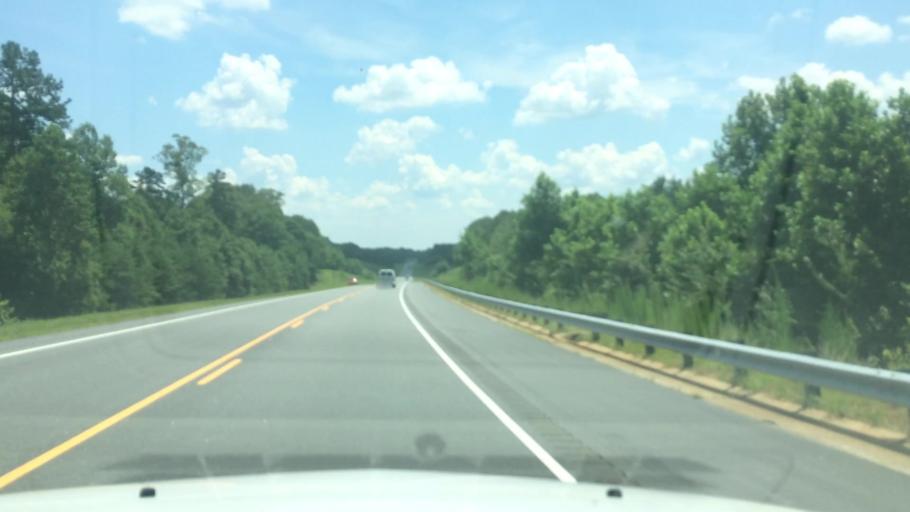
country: US
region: North Carolina
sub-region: Alexander County
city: Stony Point
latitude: 35.8845
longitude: -81.0761
